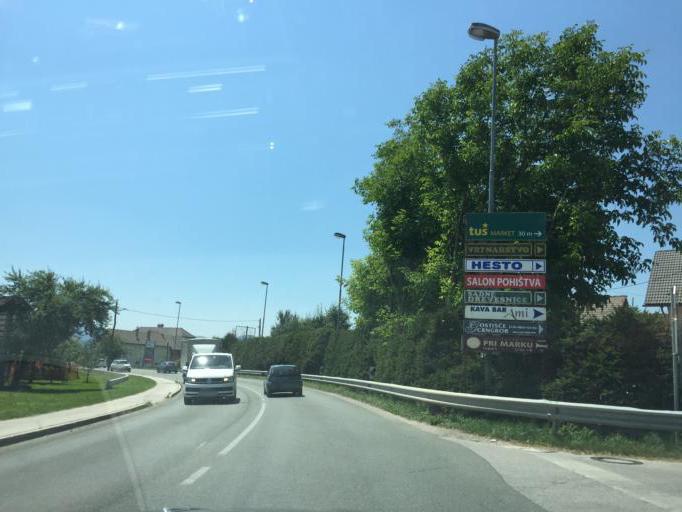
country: SI
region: Skofja Loka
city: Sv. Duh
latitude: 46.1948
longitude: 14.3249
